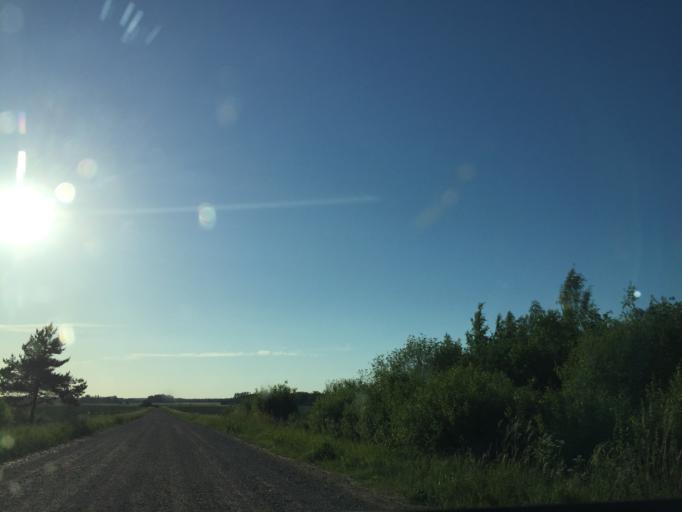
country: LV
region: Talsu Rajons
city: Sabile
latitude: 56.8745
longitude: 22.6201
